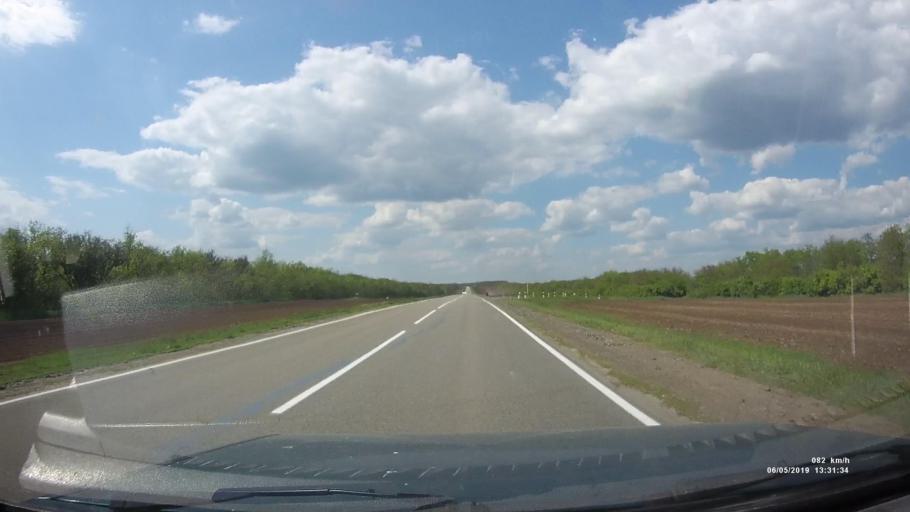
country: RU
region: Rostov
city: Ust'-Donetskiy
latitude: 47.6777
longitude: 40.8086
